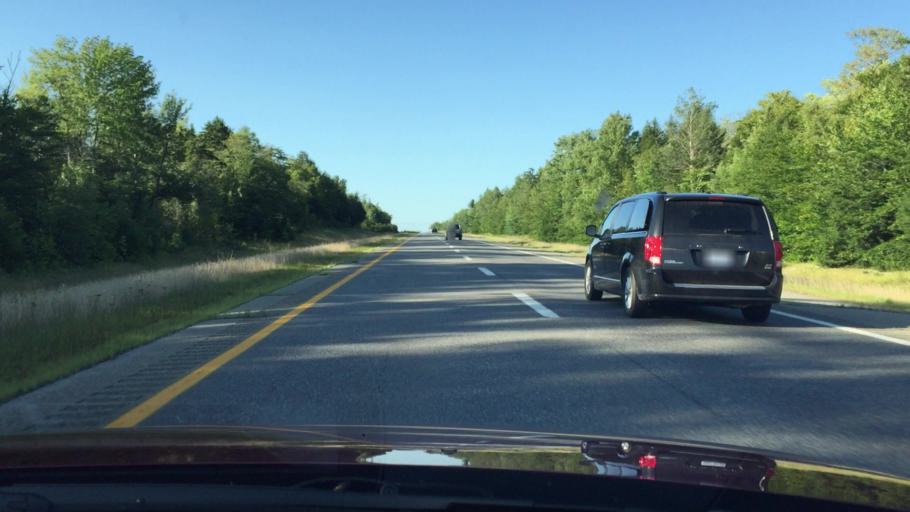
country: US
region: Maine
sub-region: Penobscot County
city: Lincoln
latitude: 45.4151
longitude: -68.5926
